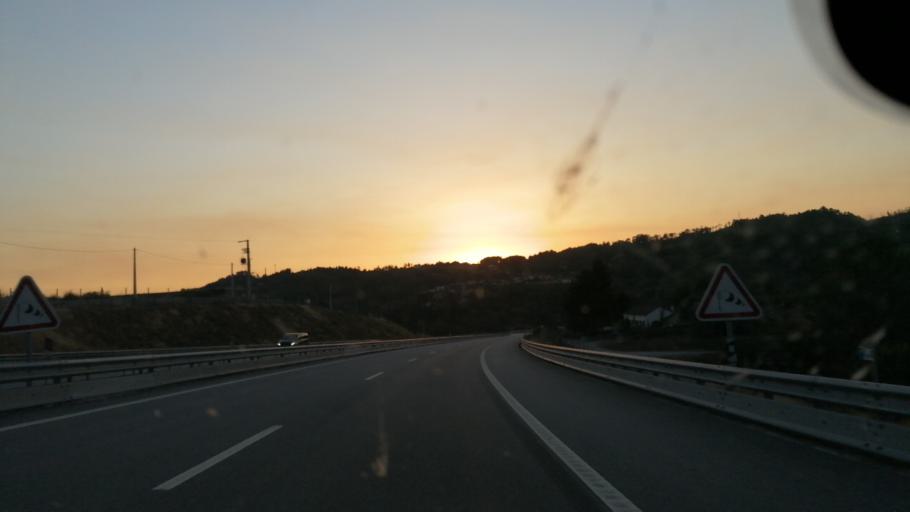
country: PT
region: Porto
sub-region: Amarante
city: Amarante
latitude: 41.2594
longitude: -8.0213
